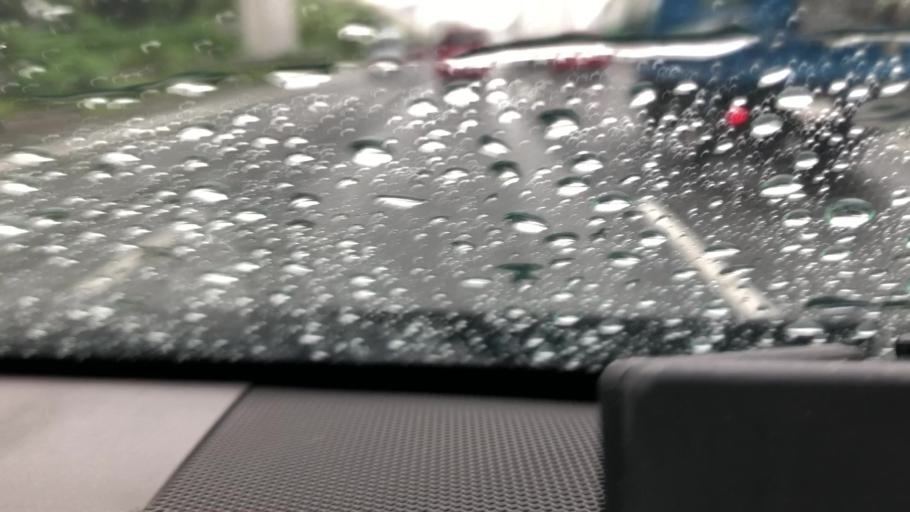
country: JP
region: Kanagawa
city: Minami-rinkan
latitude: 35.4789
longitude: 139.5213
